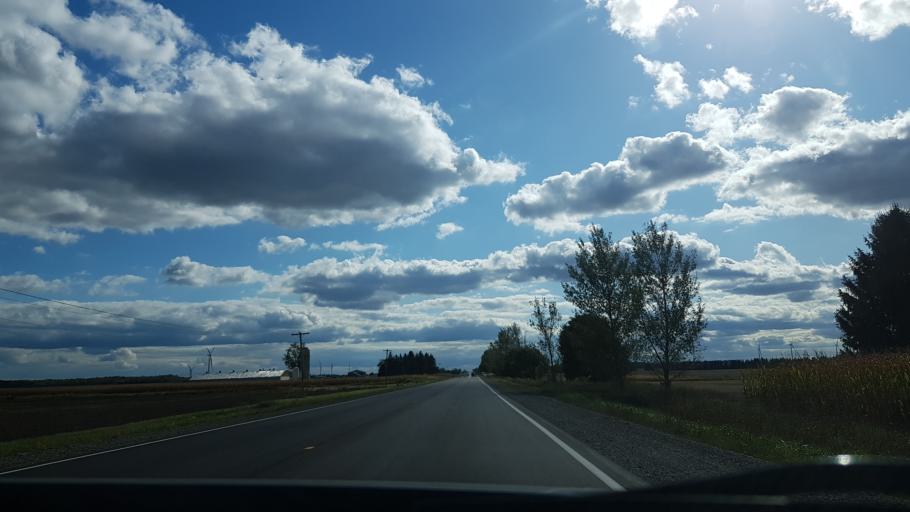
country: CA
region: Ontario
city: South Huron
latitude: 43.1280
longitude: -81.6689
